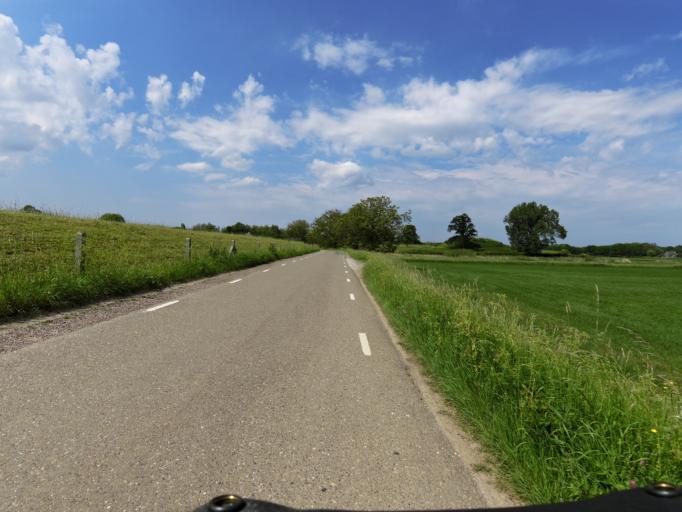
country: NL
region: North Brabant
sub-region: Gemeente Woudrichem
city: Woudrichem
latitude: 51.7910
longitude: 5.0638
